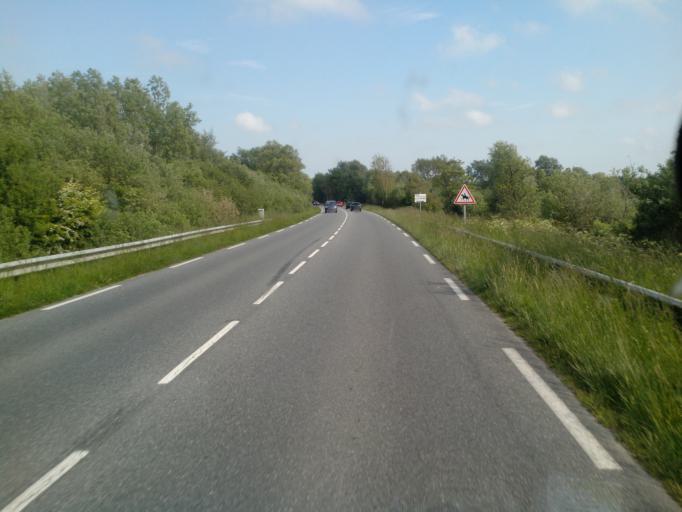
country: FR
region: Picardie
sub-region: Departement de la Somme
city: Rue
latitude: 50.2640
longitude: 1.6587
